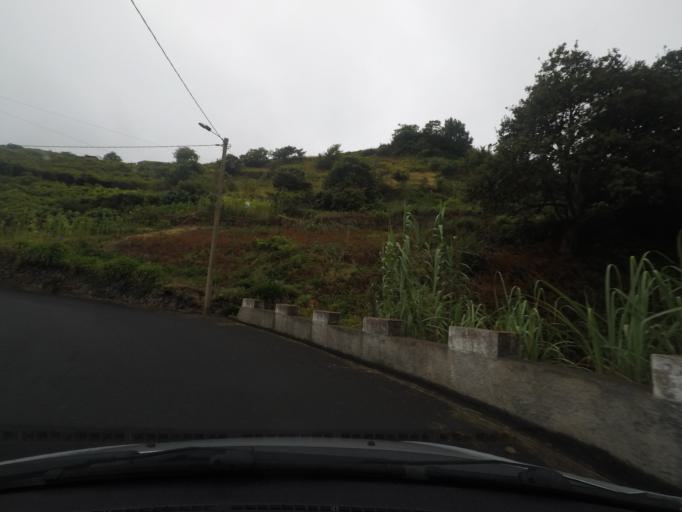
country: PT
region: Madeira
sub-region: Santana
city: Santana
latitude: 32.7853
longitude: -16.8581
